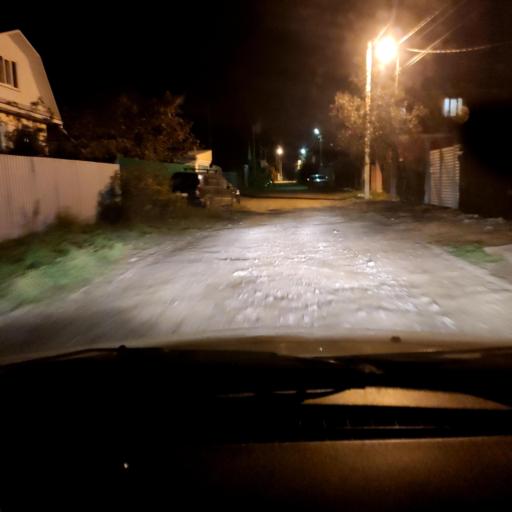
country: RU
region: Bashkortostan
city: Mikhaylovka
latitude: 54.8011
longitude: 55.9412
